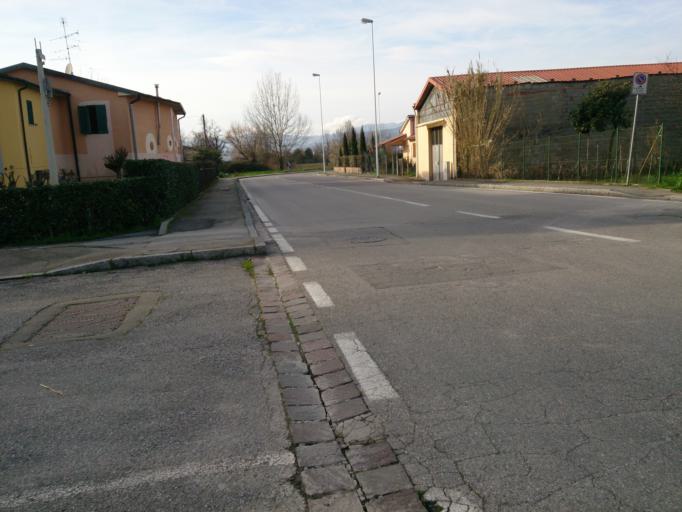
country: IT
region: Tuscany
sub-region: Provincia di Prato
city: Fornacelle
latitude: 43.8906
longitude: 11.0446
